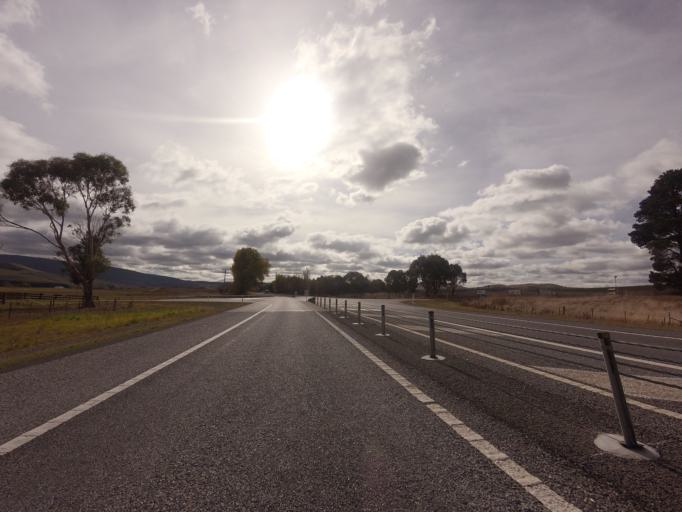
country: AU
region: Tasmania
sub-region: Brighton
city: Bridgewater
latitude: -42.4920
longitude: 147.1854
